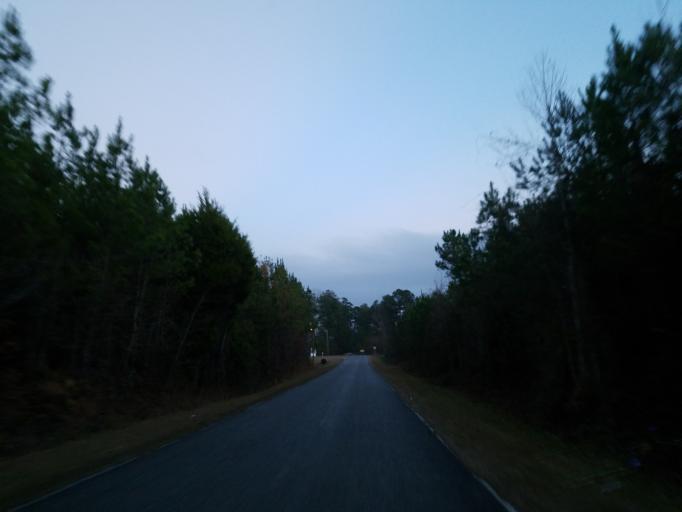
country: US
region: Alabama
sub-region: Sumter County
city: York
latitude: 32.4063
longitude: -88.4448
